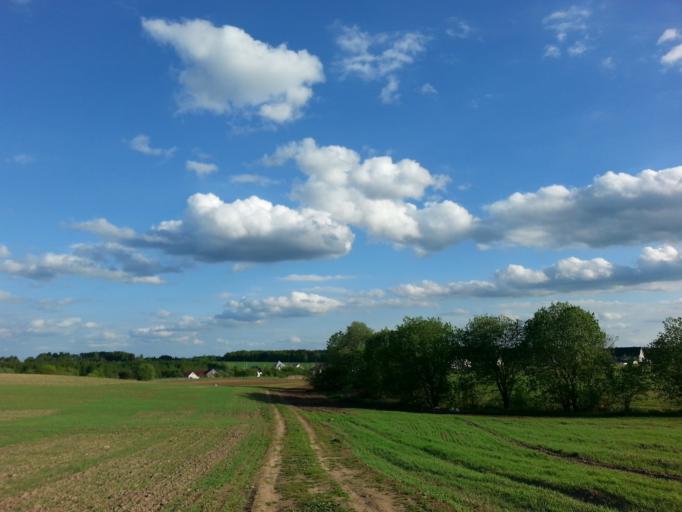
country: BY
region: Minsk
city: Narach
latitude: 54.9397
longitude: 26.7022
